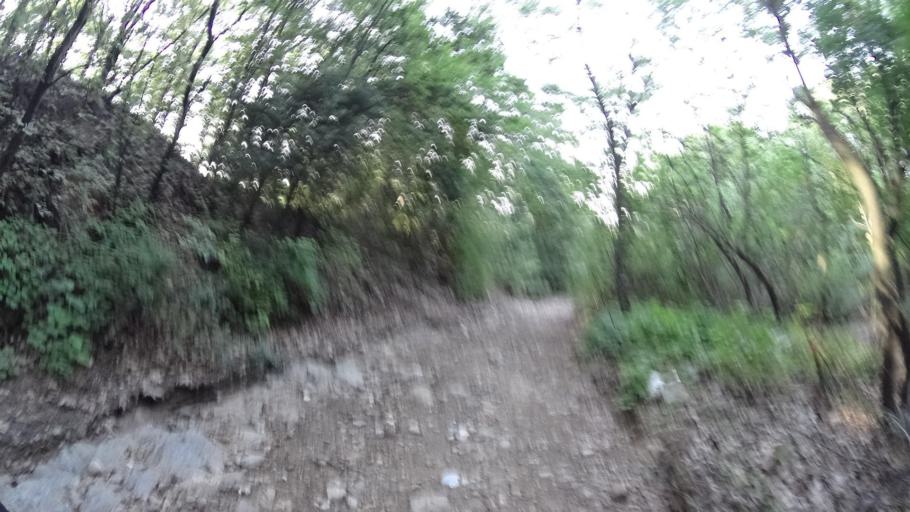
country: BG
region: Plovdiv
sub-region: Obshtina Plovdiv
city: Plovdiv
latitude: 42.0575
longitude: 24.6956
